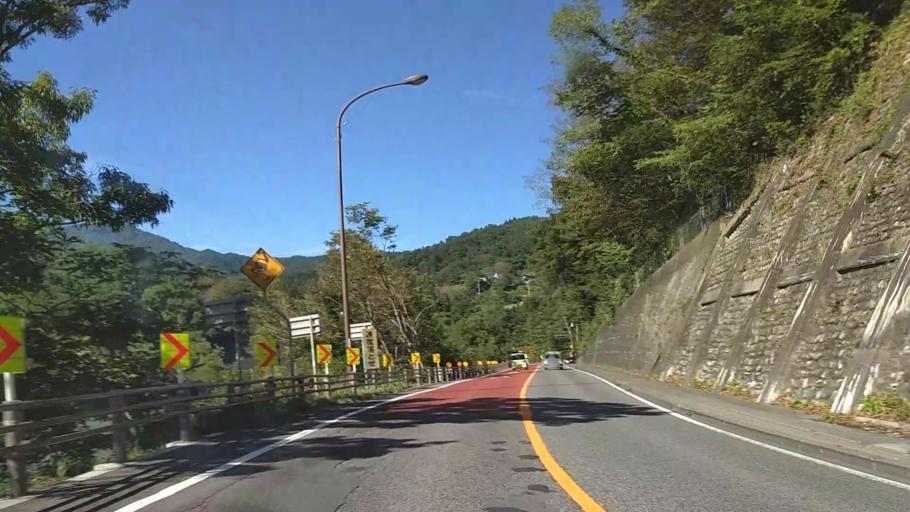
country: JP
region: Nagano
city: Nagano-shi
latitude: 36.6199
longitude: 138.1043
